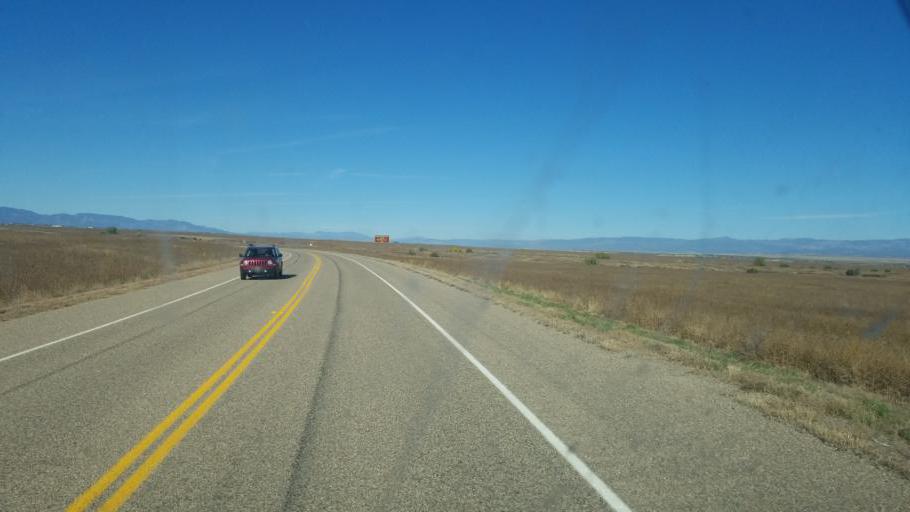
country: US
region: Colorado
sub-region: Pueblo County
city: Pueblo West
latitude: 38.2573
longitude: -104.8153
